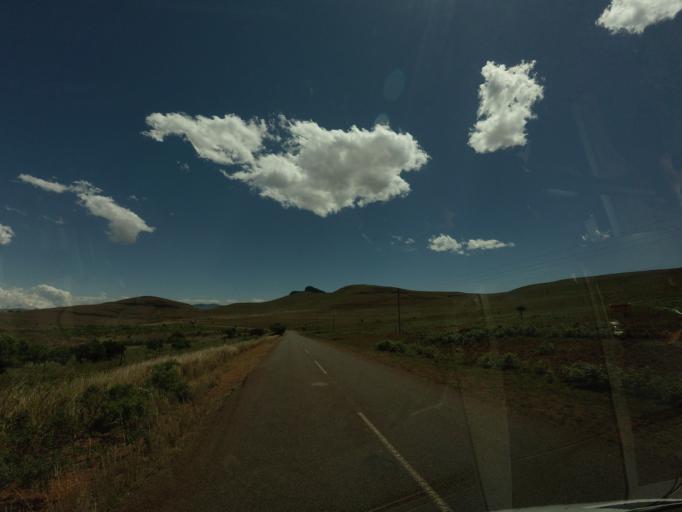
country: ZA
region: Limpopo
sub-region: Mopani District Municipality
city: Hoedspruit
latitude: -24.6229
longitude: 30.8141
